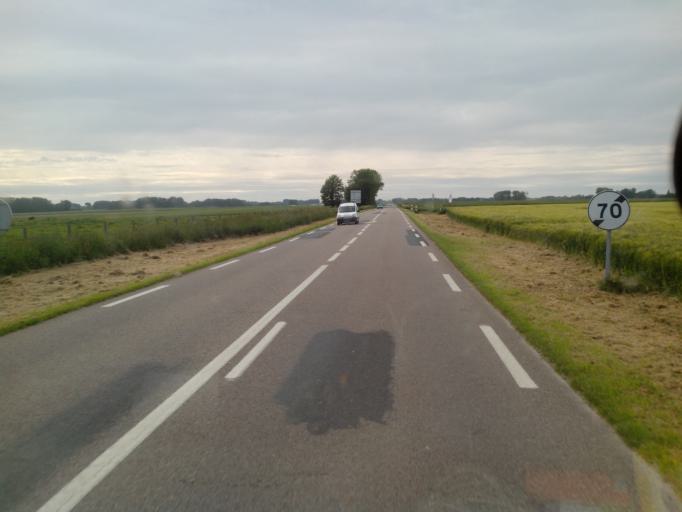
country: FR
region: Haute-Normandie
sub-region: Departement de la Seine-Maritime
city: Fauville-en-Caux
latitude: 49.6615
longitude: 0.5890
